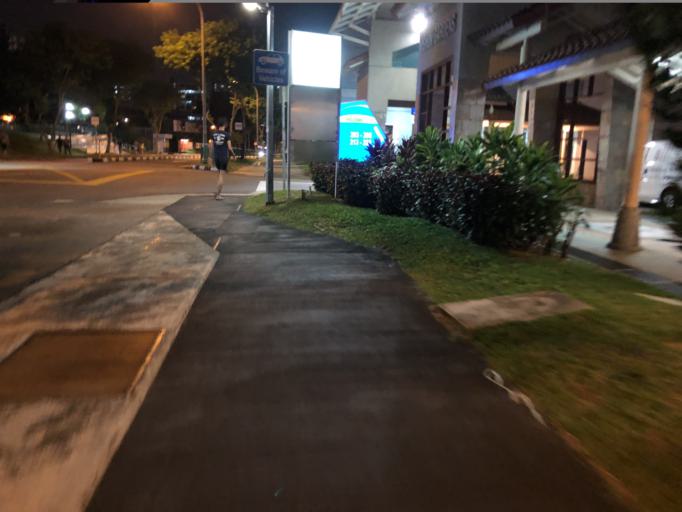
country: MY
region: Johor
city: Kampung Pasir Gudang Baru
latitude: 1.4344
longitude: 103.8363
